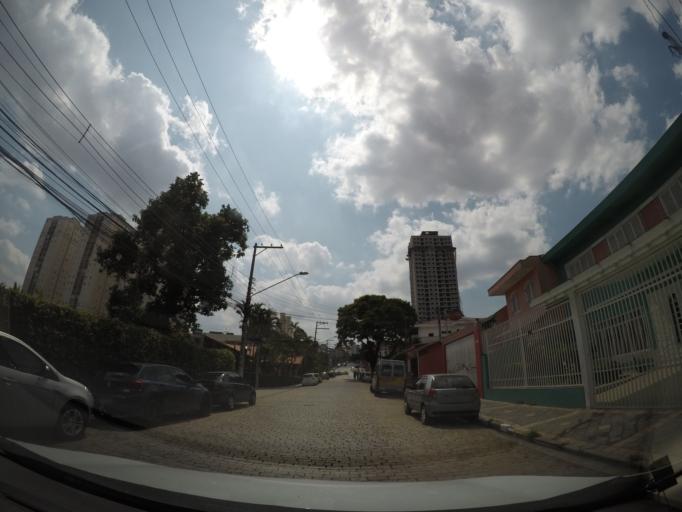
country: BR
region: Sao Paulo
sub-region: Guarulhos
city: Guarulhos
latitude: -23.4685
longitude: -46.5377
